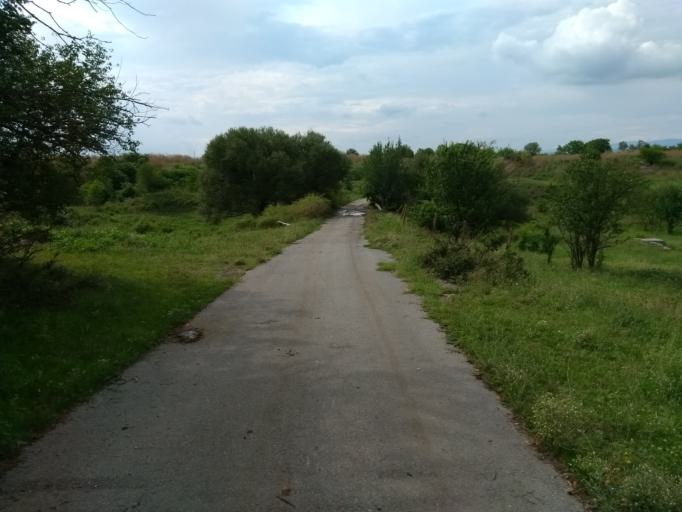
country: BG
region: Sliven
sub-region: Obshtina Sliven
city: Kermen
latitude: 42.4607
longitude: 26.1383
